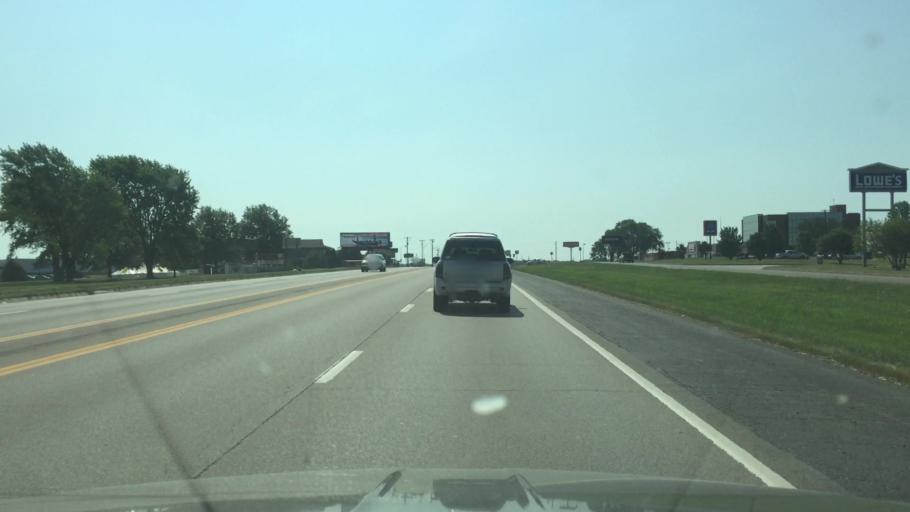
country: US
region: Missouri
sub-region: Pettis County
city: Sedalia
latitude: 38.7125
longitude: -93.2765
